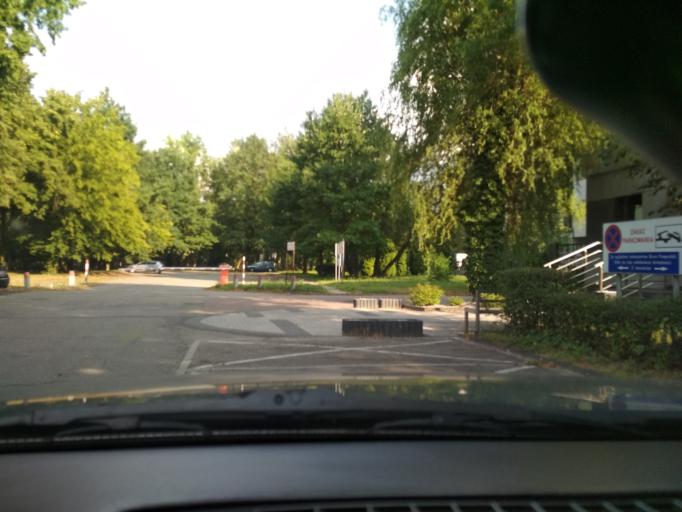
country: PL
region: Silesian Voivodeship
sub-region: Gliwice
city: Gliwice
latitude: 50.2967
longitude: 18.6358
